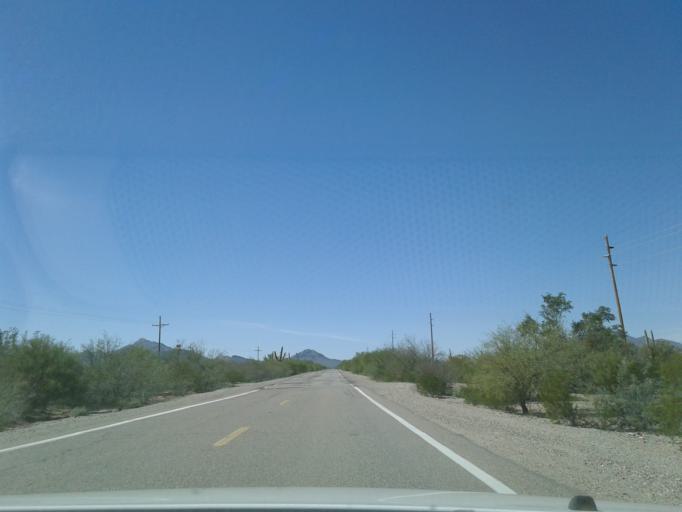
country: US
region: Arizona
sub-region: Pima County
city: Avra Valley
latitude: 32.3710
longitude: -111.3857
